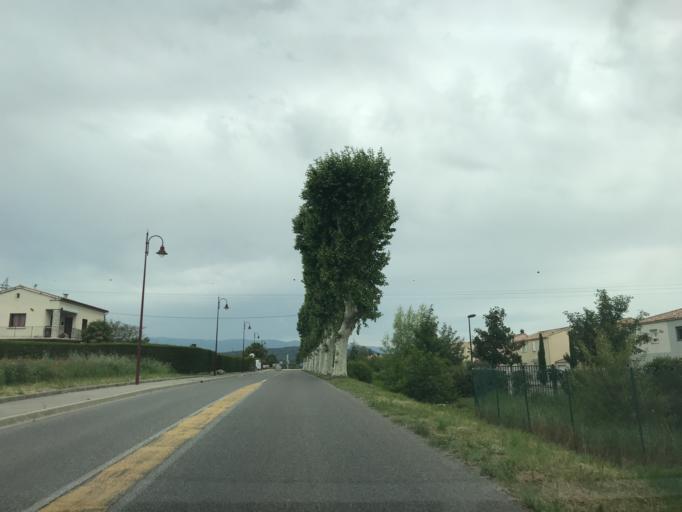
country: FR
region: Provence-Alpes-Cote d'Azur
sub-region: Departement des Alpes-de-Haute-Provence
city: Oraison
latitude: 43.9297
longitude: 5.8906
